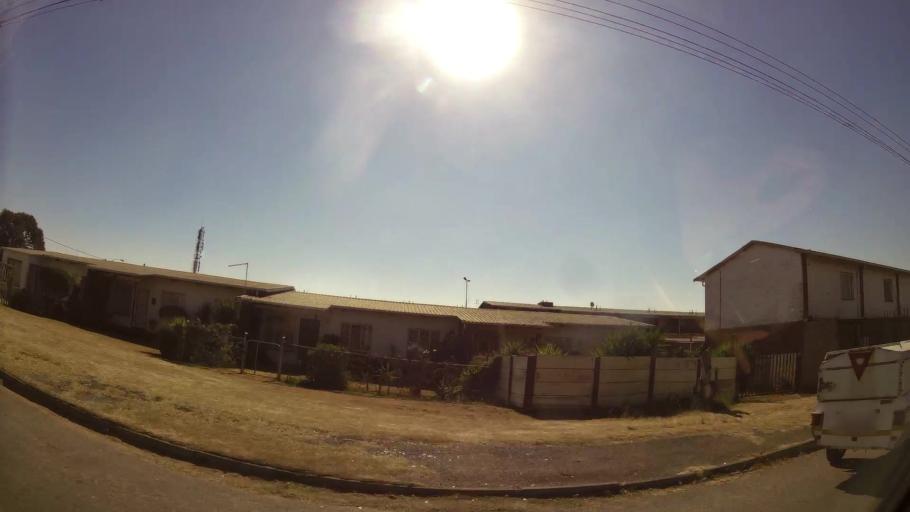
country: ZA
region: Gauteng
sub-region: City of Johannesburg Metropolitan Municipality
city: Johannesburg
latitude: -26.2448
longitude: 28.0928
